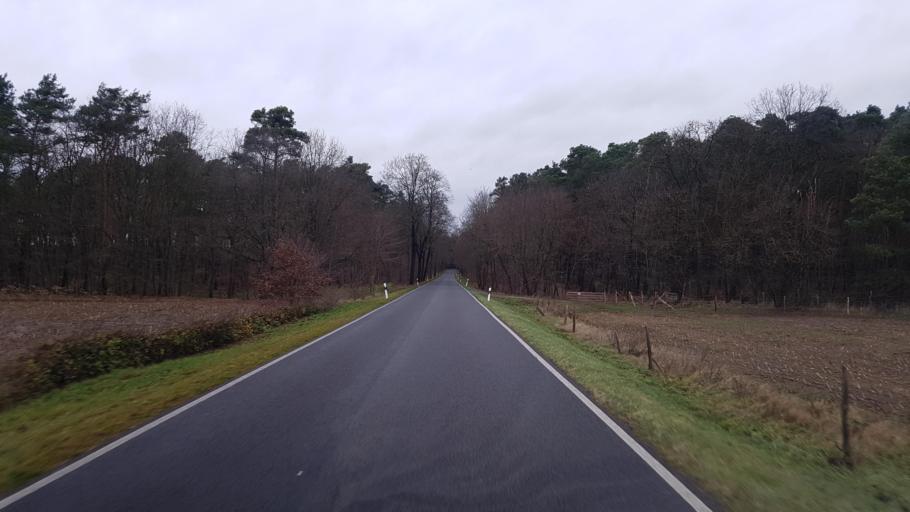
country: DE
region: Brandenburg
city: Tauche
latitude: 52.0914
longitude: 14.1689
